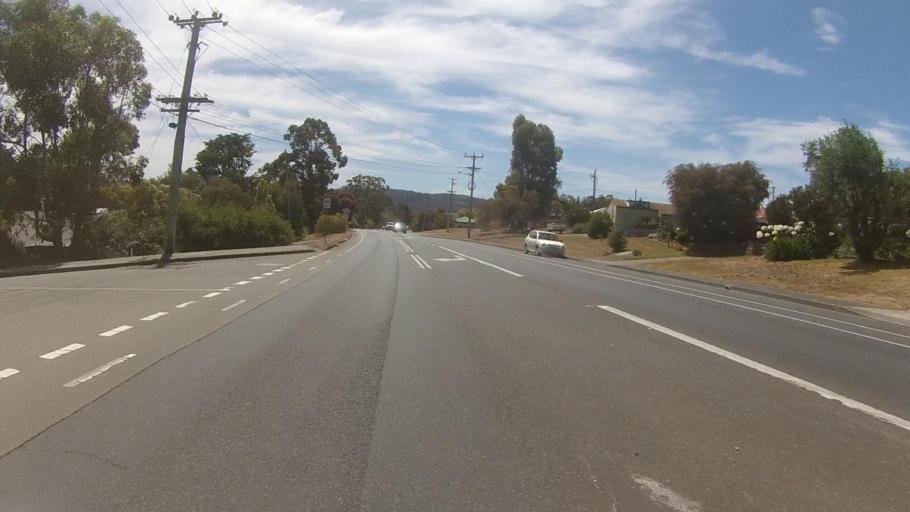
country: AU
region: Tasmania
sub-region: Kingborough
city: Kingston
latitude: -42.9813
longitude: 147.2976
